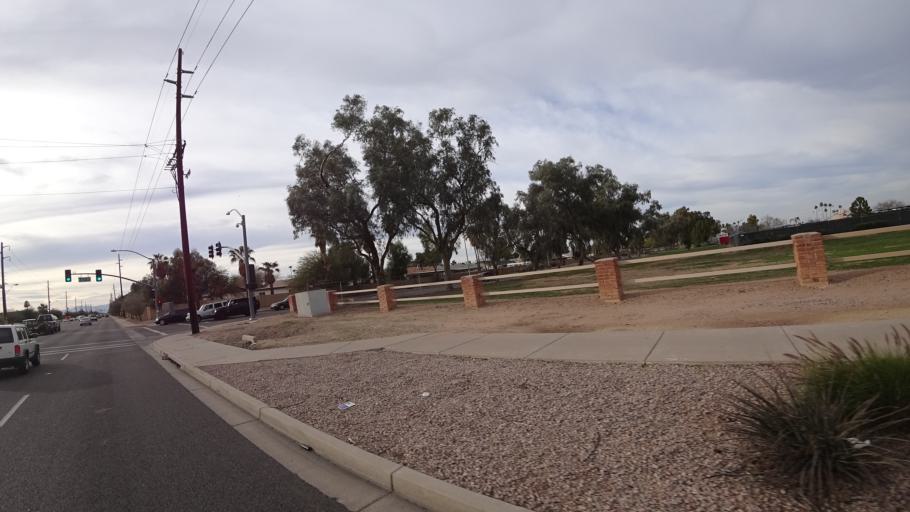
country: US
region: Arizona
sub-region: Maricopa County
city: Glendale
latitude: 33.5674
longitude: -112.1944
